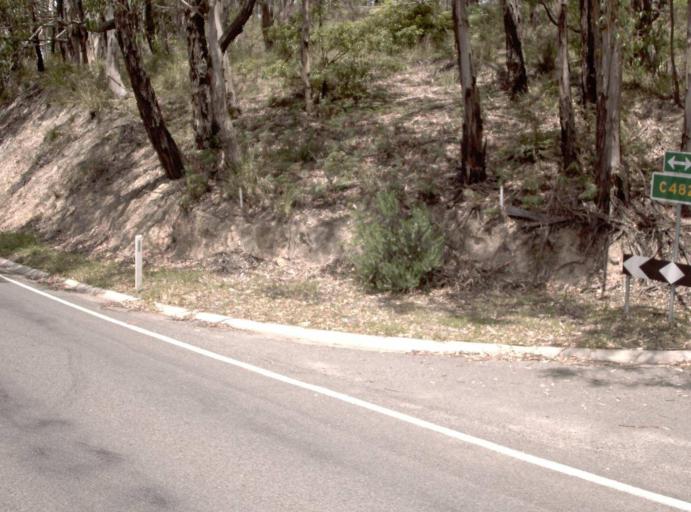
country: AU
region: Victoria
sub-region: Latrobe
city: Traralgon
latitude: -38.3618
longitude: 146.7584
